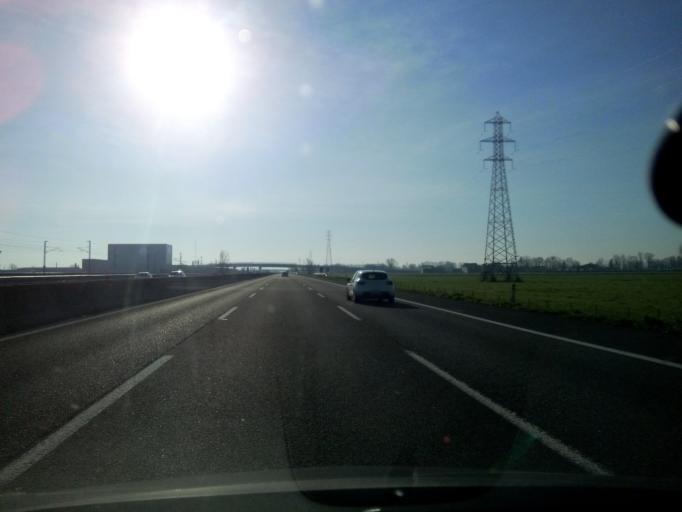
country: IT
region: Emilia-Romagna
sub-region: Provincia di Reggio Emilia
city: Prato
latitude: 44.6985
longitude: 10.7553
